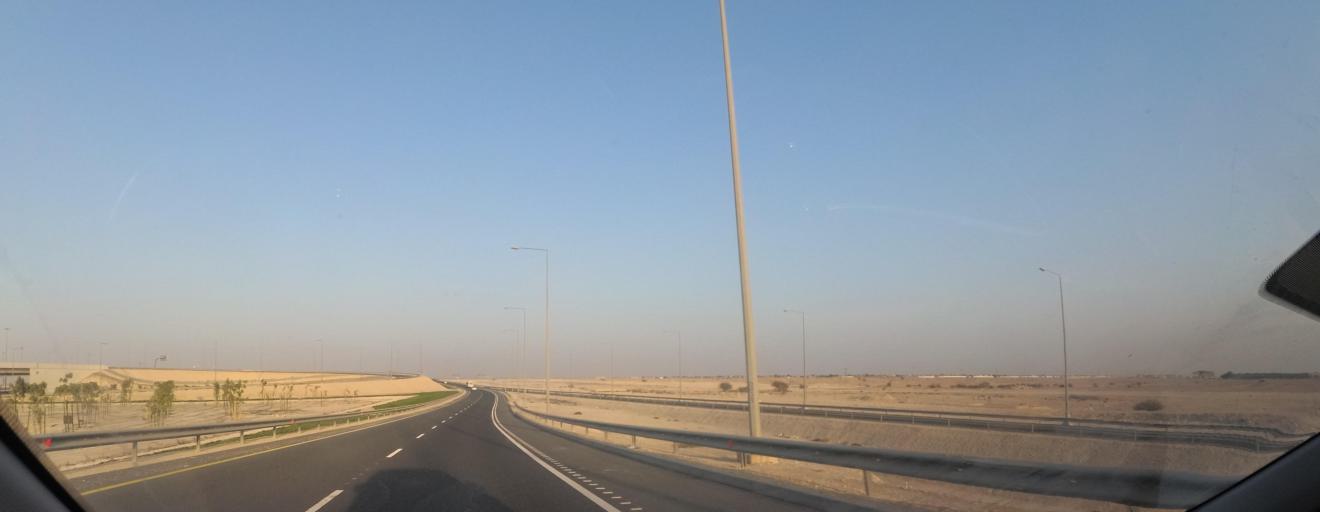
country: QA
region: Baladiyat az Za`ayin
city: Az Za`ayin
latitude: 25.6148
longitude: 51.3675
